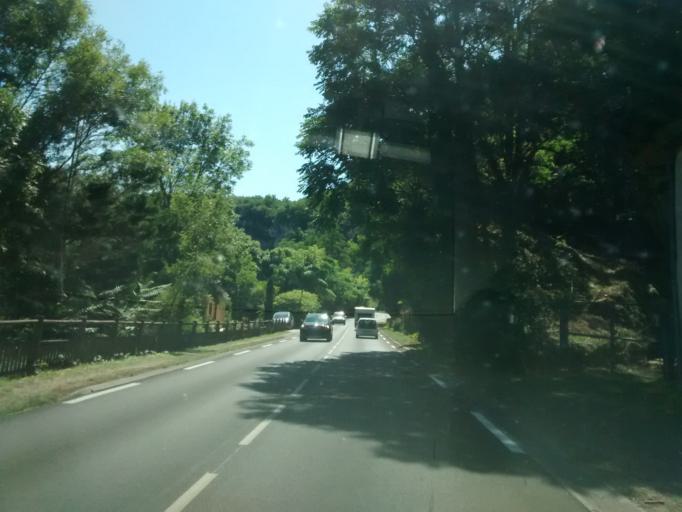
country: FR
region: Aquitaine
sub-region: Departement de la Dordogne
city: Le Bugue
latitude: 44.9526
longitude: 1.0026
